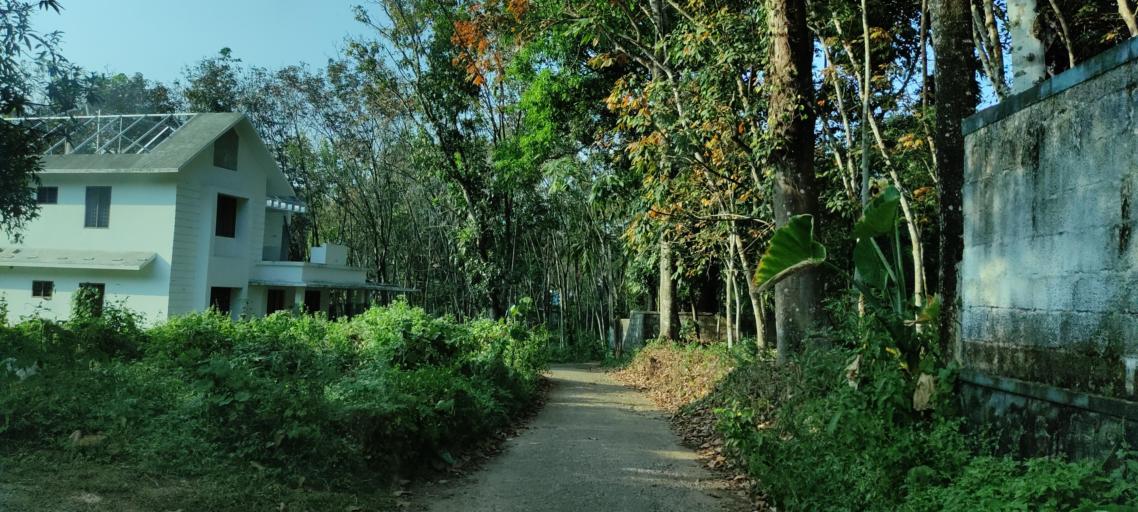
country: IN
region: Kerala
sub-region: Pattanamtitta
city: Adur
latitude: 9.1508
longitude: 76.7585
